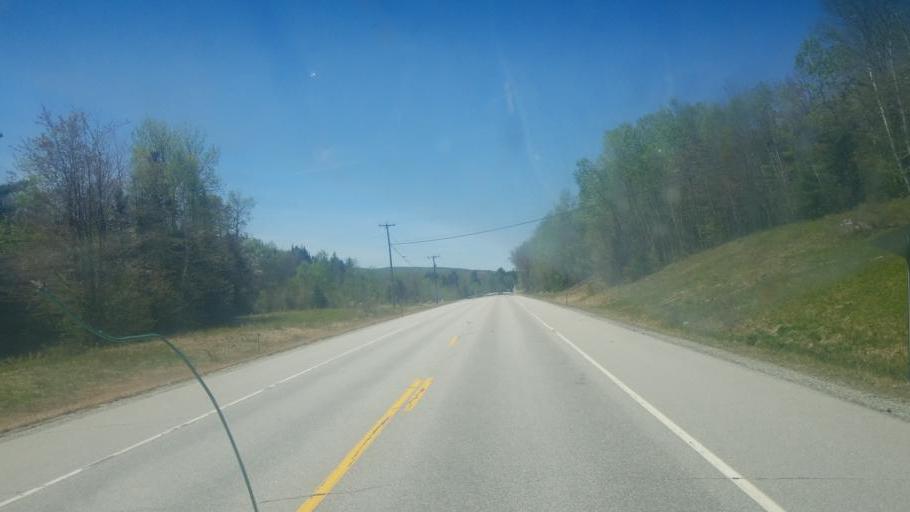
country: US
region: New Hampshire
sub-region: Grafton County
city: Deerfield
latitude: 44.2706
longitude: -71.5206
